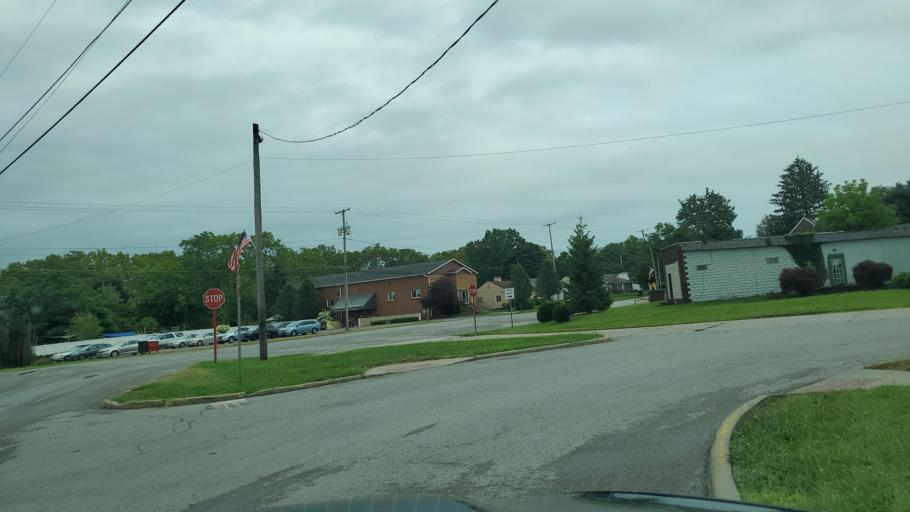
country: US
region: Ohio
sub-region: Trumbull County
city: McDonald
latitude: 41.1687
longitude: -80.7247
